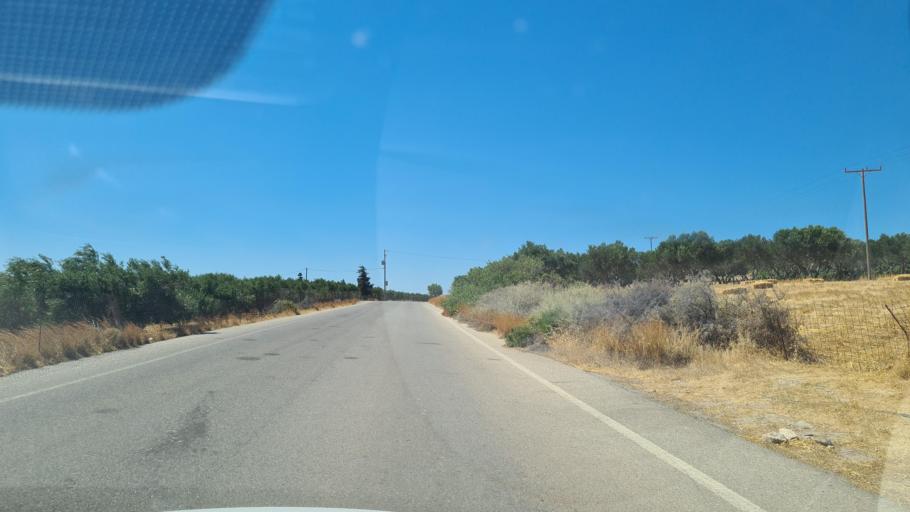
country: GR
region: Crete
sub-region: Nomos Chanias
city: Palaiochora
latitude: 35.2982
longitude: 23.5401
